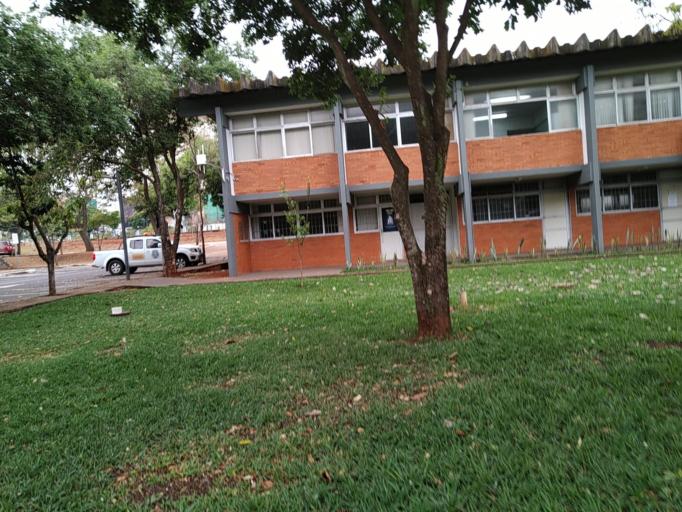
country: BR
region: Minas Gerais
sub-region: Uberlandia
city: Uberlandia
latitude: -18.9187
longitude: -48.2556
